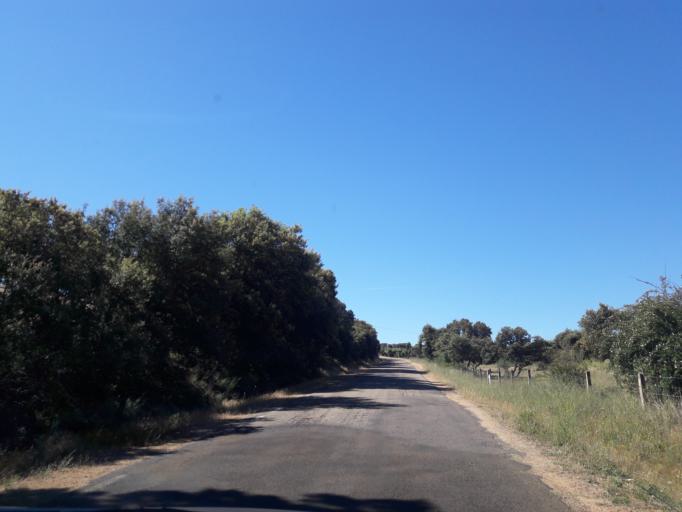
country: ES
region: Castille and Leon
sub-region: Provincia de Salamanca
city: Vega de Tirados
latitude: 41.0570
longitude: -5.8910
